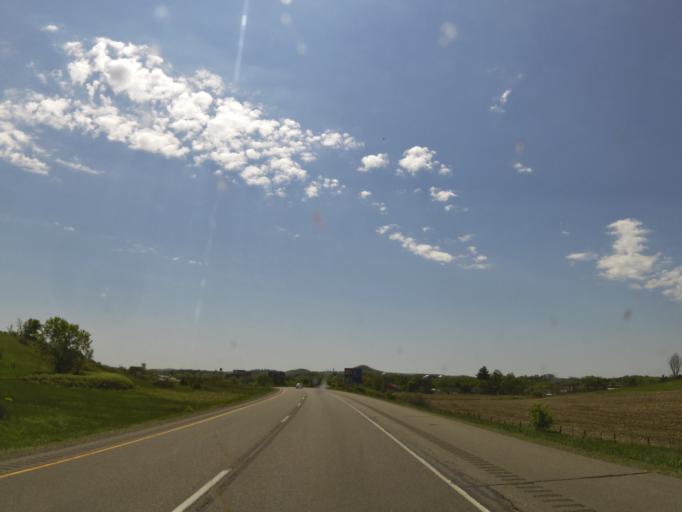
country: US
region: Wisconsin
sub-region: Jackson County
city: Black River Falls
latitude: 44.3927
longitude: -91.0118
